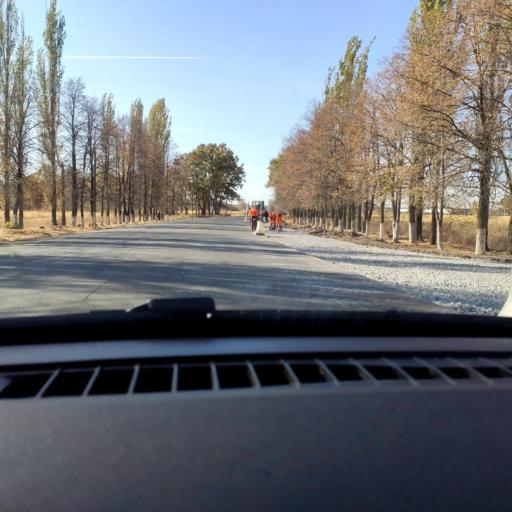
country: RU
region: Voronezj
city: Podgornoye
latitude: 51.8014
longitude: 39.2102
